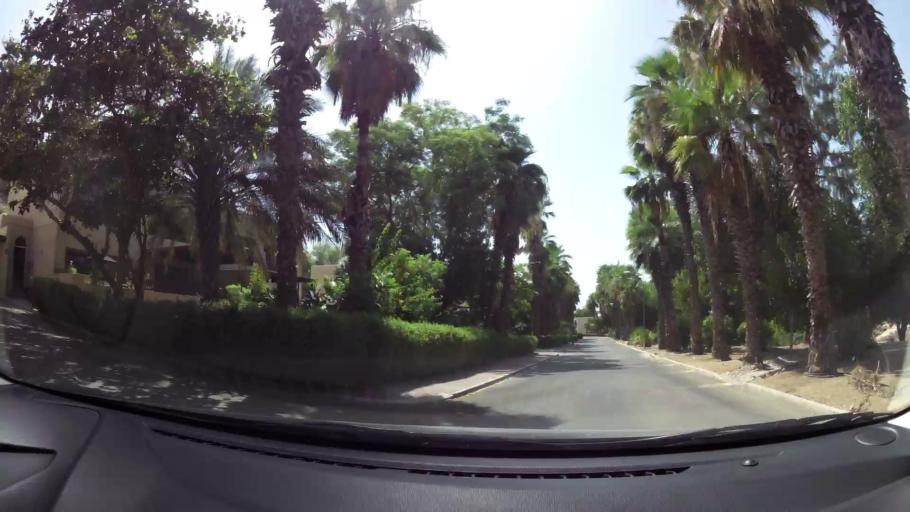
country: OM
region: Muhafazat Masqat
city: Muscat
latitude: 23.6314
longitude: 58.4951
